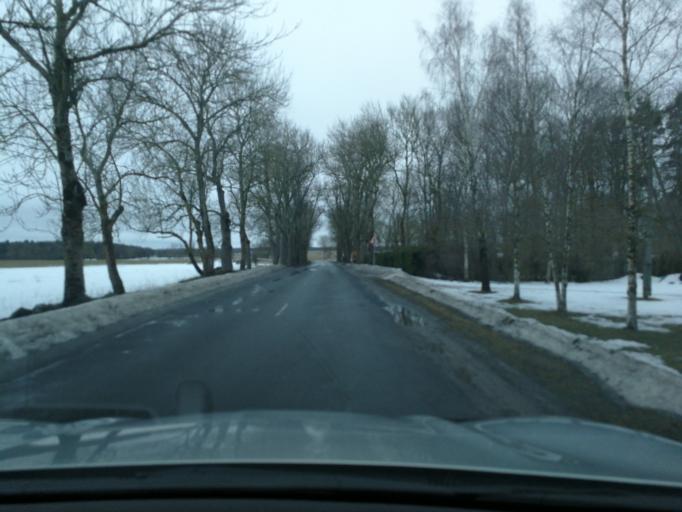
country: EE
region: Harju
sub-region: Kiili vald
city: Kiili
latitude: 59.2750
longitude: 24.8748
